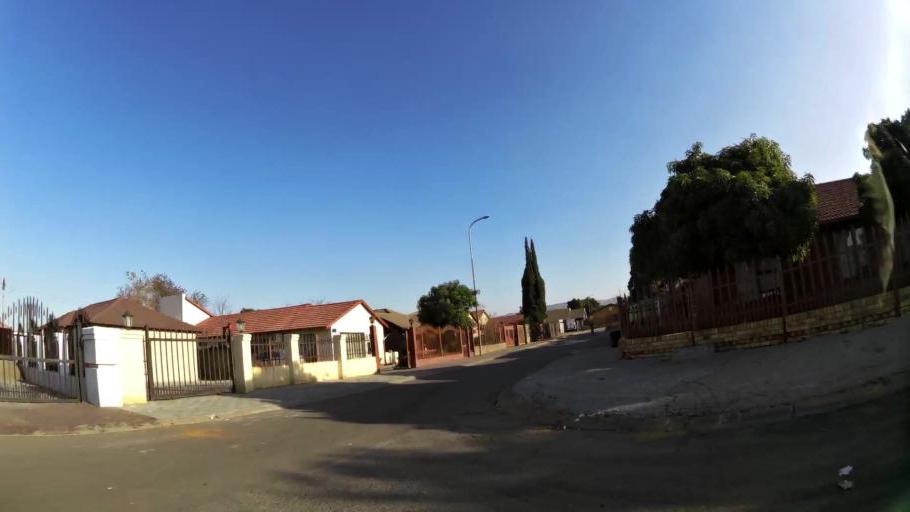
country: ZA
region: North-West
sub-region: Bojanala Platinum District Municipality
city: Rustenburg
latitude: -25.6456
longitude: 27.2262
